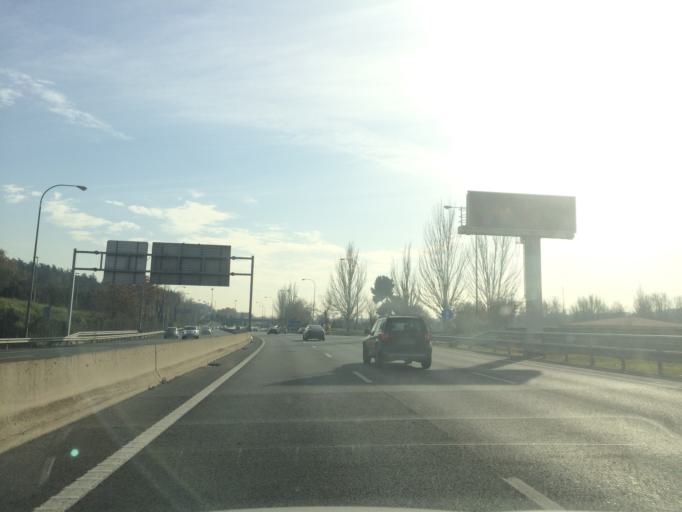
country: ES
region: Madrid
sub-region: Provincia de Madrid
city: Moncloa-Aravaca
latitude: 40.4495
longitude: -3.7415
